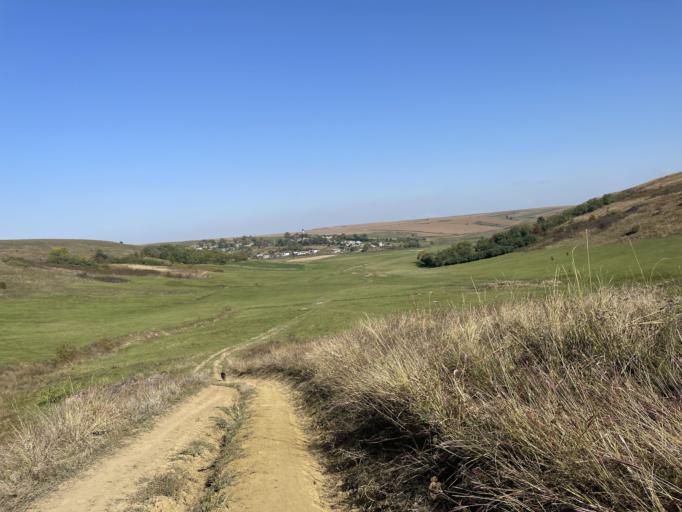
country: RO
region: Iasi
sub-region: Comuna Dumesti
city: Pausesti
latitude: 47.1543
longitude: 27.3089
